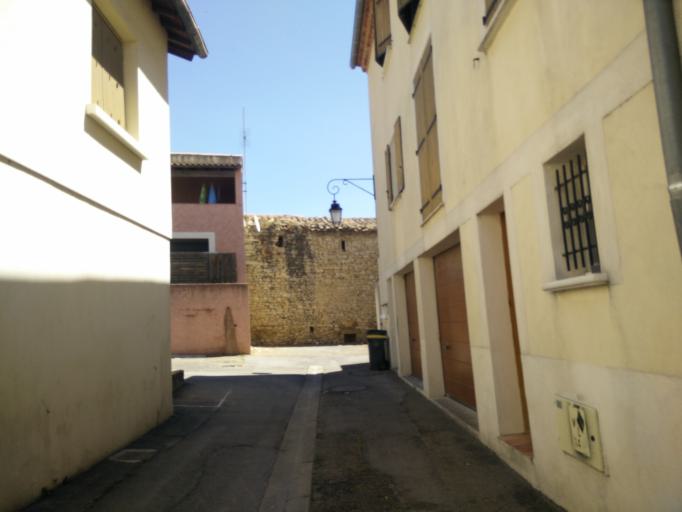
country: FR
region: Languedoc-Roussillon
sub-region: Departement du Gard
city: Uchaud
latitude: 43.7579
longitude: 4.2694
